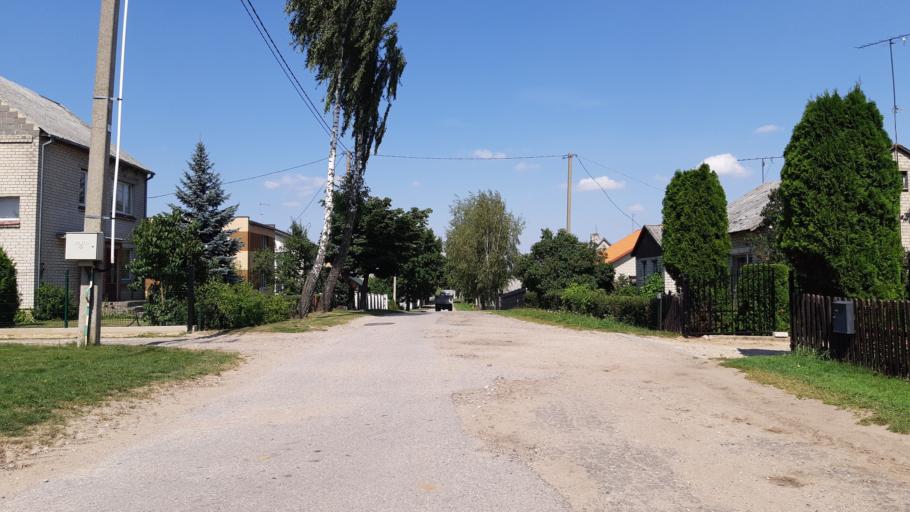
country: LT
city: Virbalis
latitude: 54.6217
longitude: 22.8170
